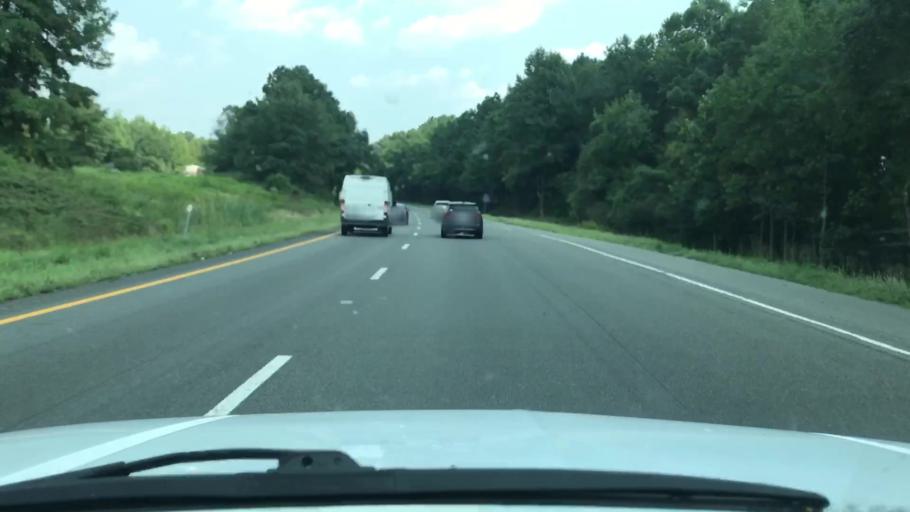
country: US
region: Virginia
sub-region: Henrico County
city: Chamberlayne
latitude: 37.6533
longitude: -77.4391
